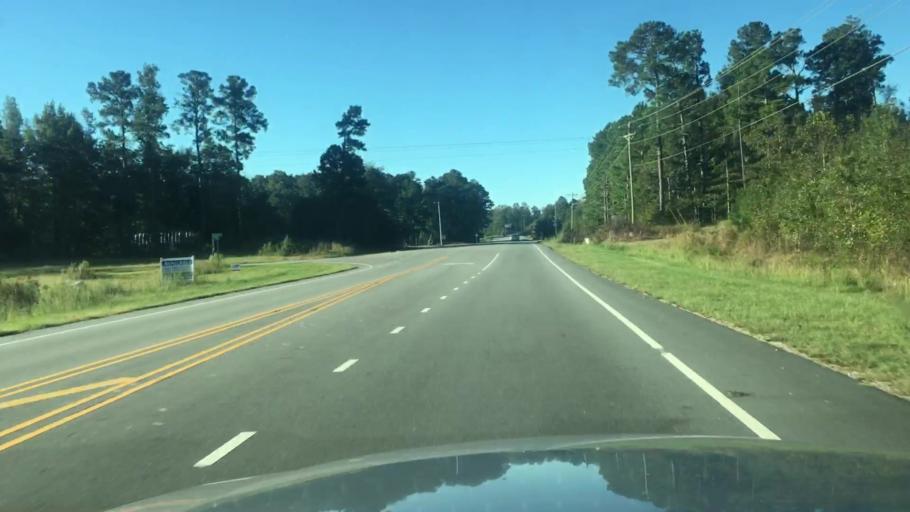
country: US
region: North Carolina
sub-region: Cumberland County
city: Spring Lake
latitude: 35.2569
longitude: -78.9250
